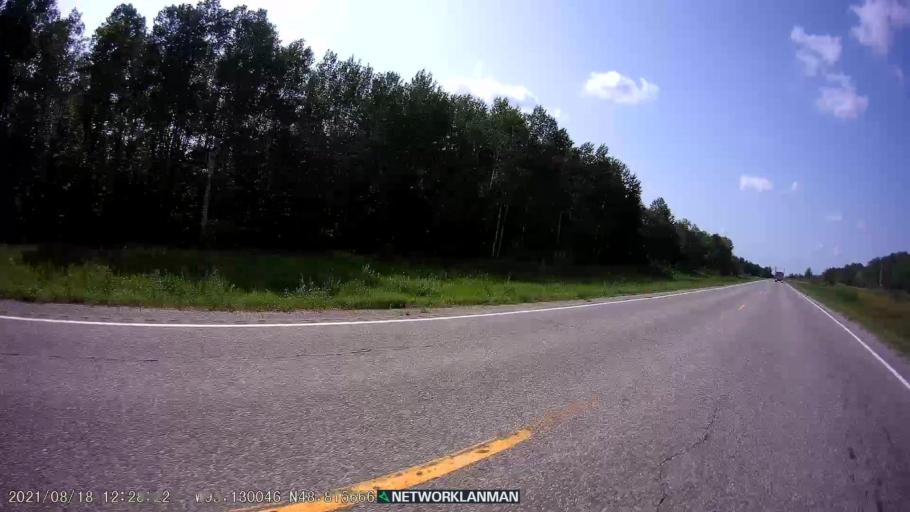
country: US
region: Minnesota
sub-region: Roseau County
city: Warroad
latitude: 48.8159
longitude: -95.1312
